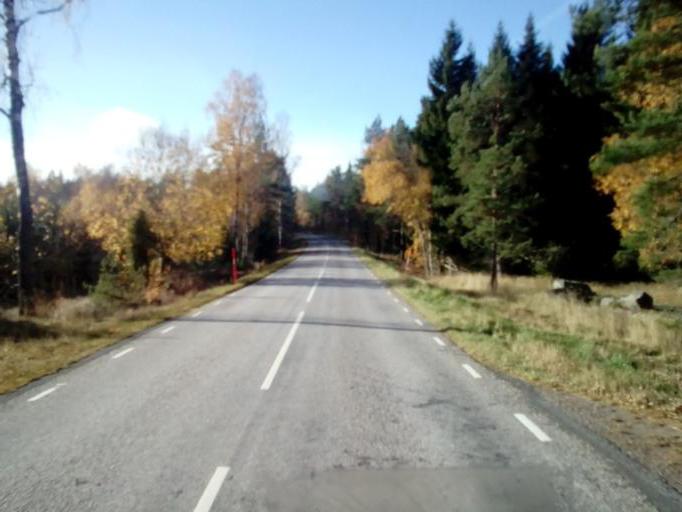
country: SE
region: Kalmar
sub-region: Vasterviks Kommun
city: Ankarsrum
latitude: 57.7707
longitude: 16.1430
